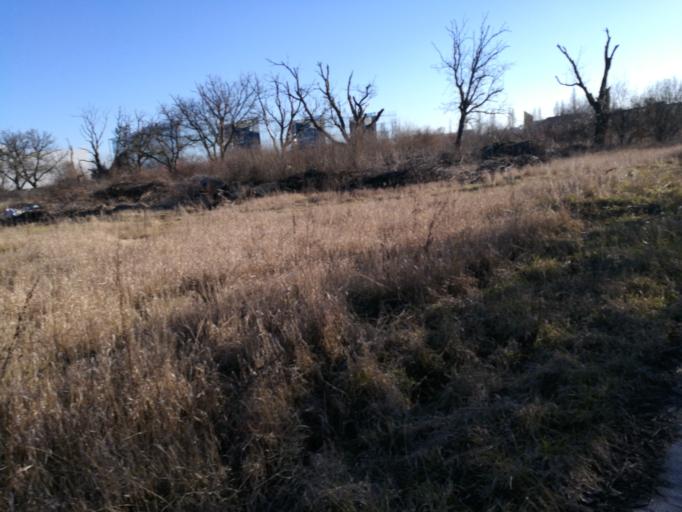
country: RO
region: Ilfov
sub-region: Comuna Otopeni
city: Otopeni
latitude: 44.5066
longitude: 26.0781
